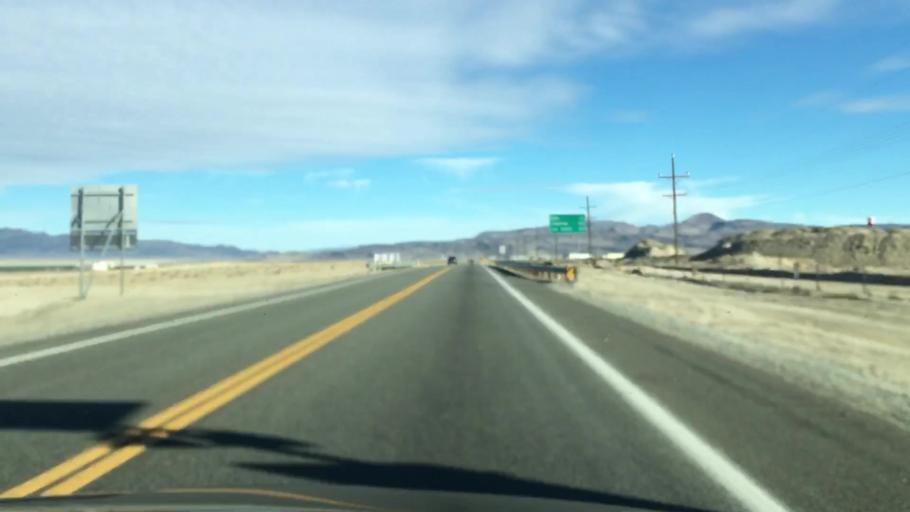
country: US
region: Nevada
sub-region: Mineral County
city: Hawthorne
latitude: 38.5245
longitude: -118.6072
